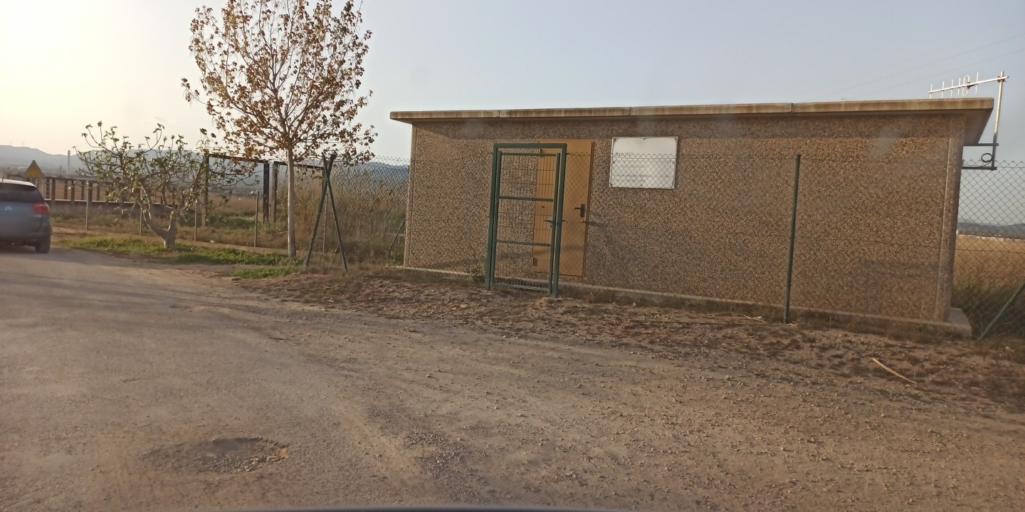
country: ES
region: Catalonia
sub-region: Provincia de Tarragona
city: L'Ampolla
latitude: 40.7853
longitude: 0.7026
